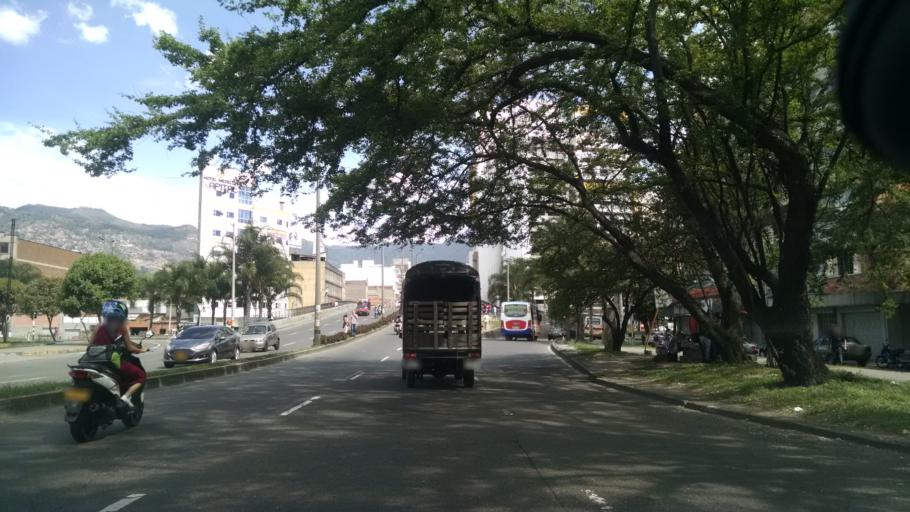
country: CO
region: Antioquia
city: Medellin
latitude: 6.2535
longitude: -75.5761
